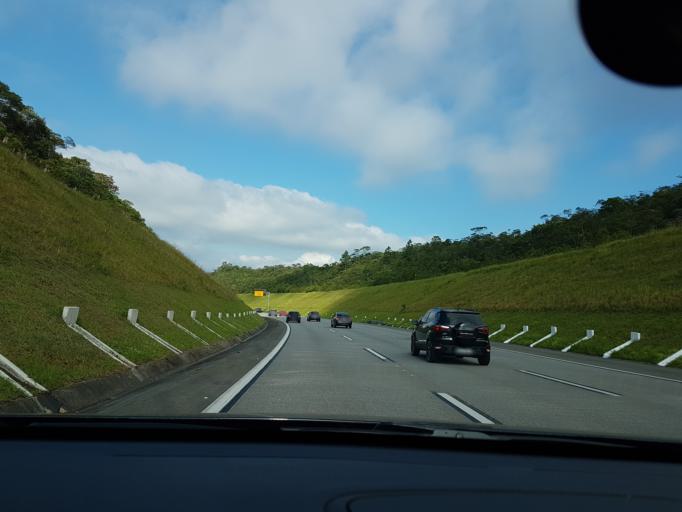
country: BR
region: Sao Paulo
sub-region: Cubatao
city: Cubatao
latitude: -23.9287
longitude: -46.5491
